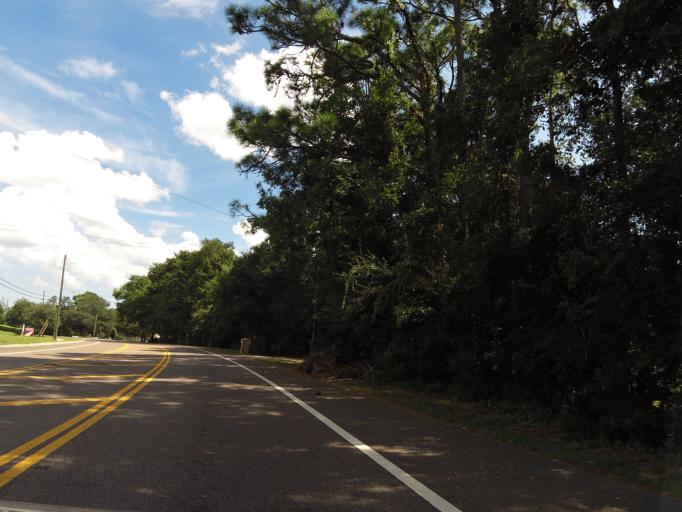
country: US
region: Florida
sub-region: Duval County
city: Jacksonville
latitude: 30.4261
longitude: -81.5799
